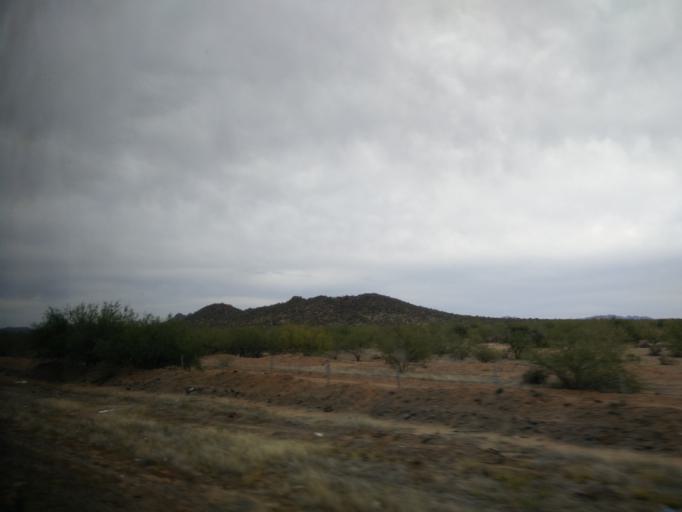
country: MX
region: Sonora
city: Hermosillo
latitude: 28.8426
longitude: -110.9582
